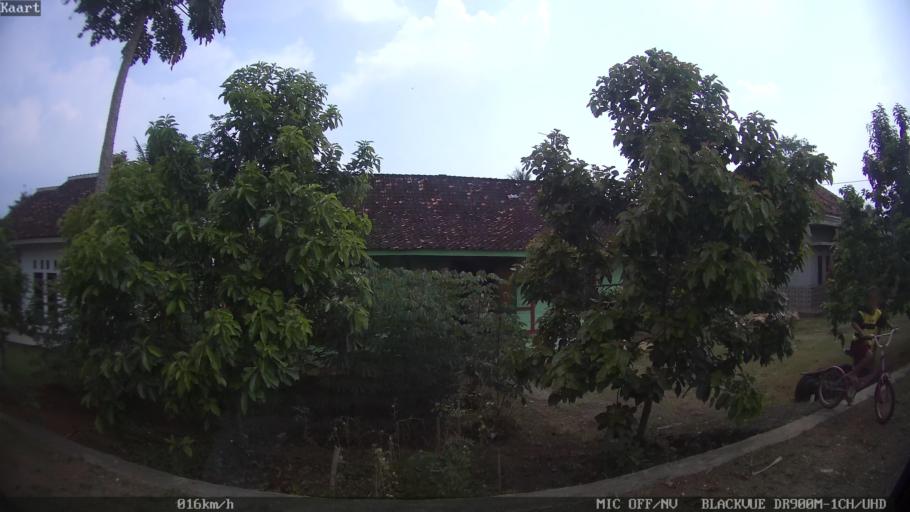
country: ID
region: Lampung
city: Gadingrejo
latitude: -5.3690
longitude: 105.0635
